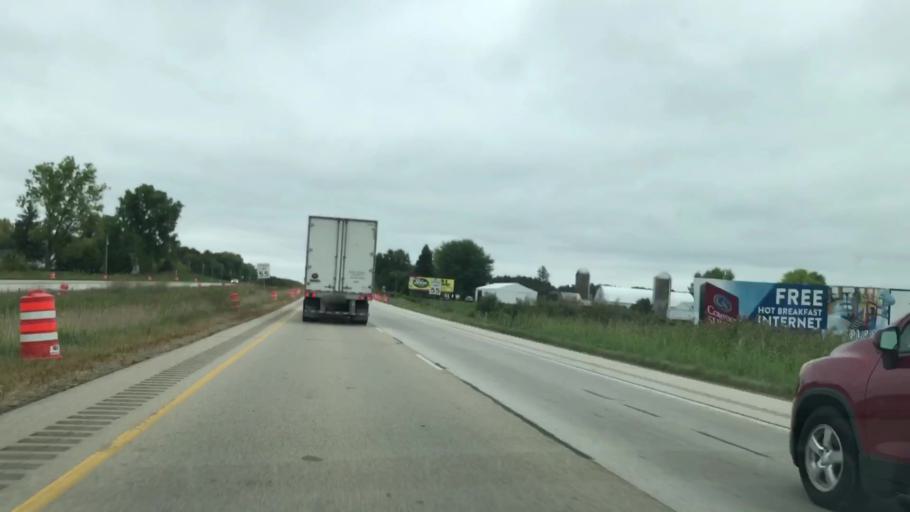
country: US
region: Wisconsin
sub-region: Brown County
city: Suamico
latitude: 44.6590
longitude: -88.0502
